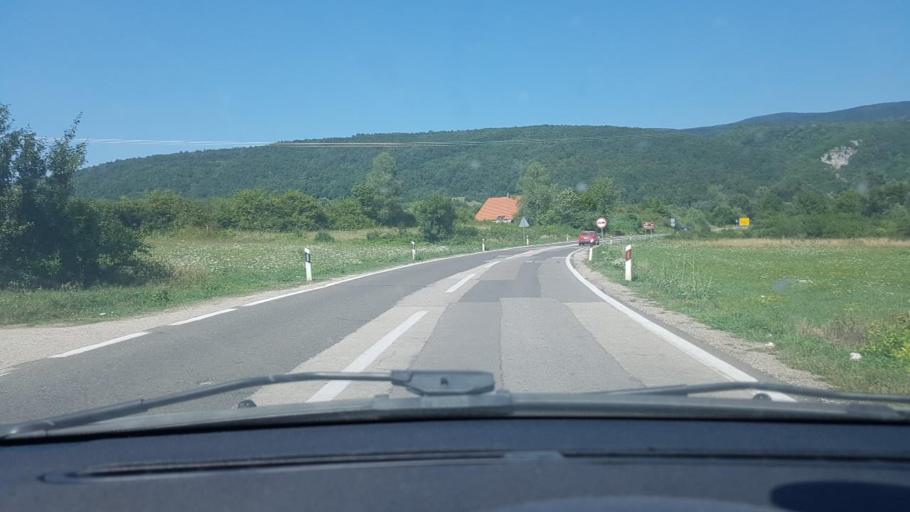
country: BA
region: Federation of Bosnia and Herzegovina
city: Bihac
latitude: 44.7705
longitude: 15.9447
